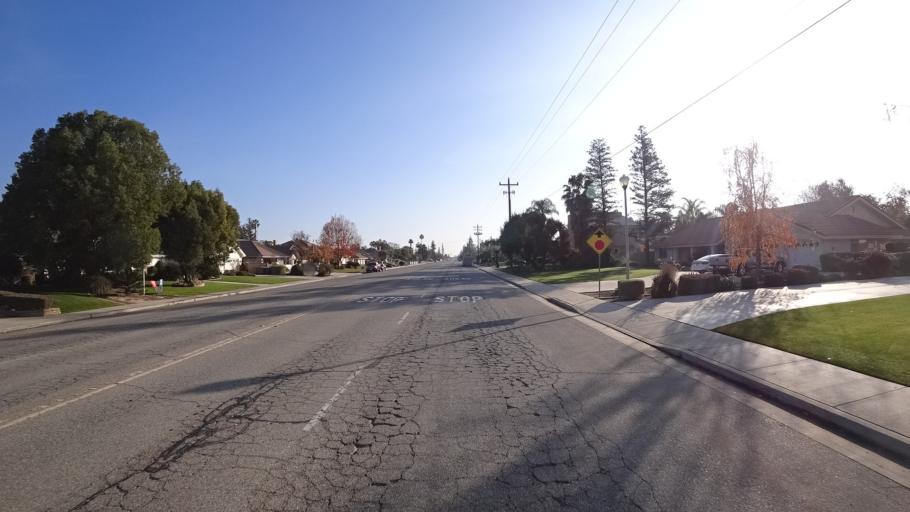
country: US
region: California
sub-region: Kern County
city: Rosedale
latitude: 35.3762
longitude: -119.1393
